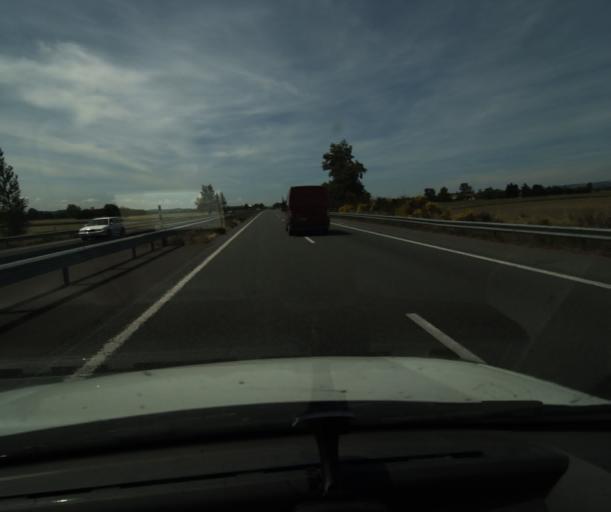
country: FR
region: Languedoc-Roussillon
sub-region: Departement de l'Aude
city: Saint-Martin-Lalande
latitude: 43.2616
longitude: 2.0223
